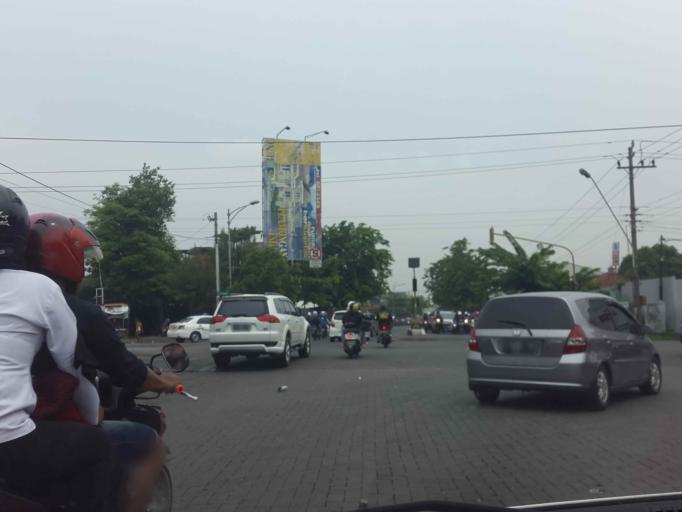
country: ID
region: Central Java
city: Semarang
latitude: -6.9697
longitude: 110.4336
